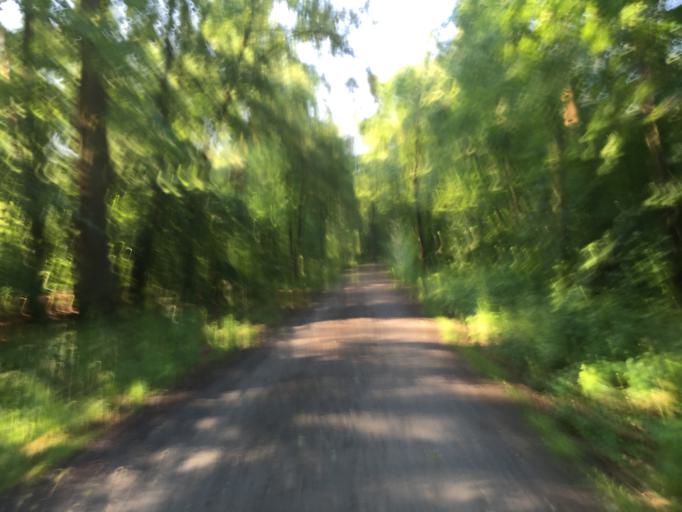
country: DE
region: Hesse
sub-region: Regierungsbezirk Darmstadt
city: Darmstadt
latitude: 49.8665
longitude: 8.6193
